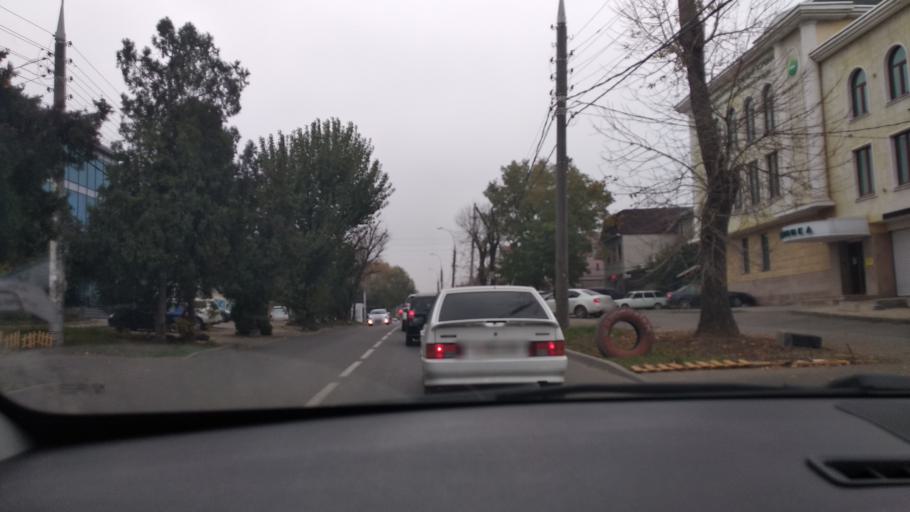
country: RU
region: Krasnodarskiy
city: Krasnodar
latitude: 45.0225
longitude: 39.0096
